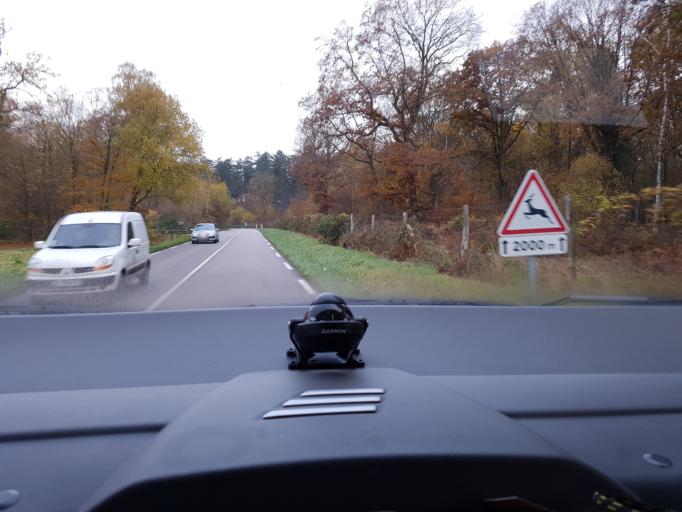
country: FR
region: Haute-Normandie
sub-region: Departement de la Seine-Maritime
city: Saint-Pierre-de-Varengeville
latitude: 49.4973
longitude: 0.9138
